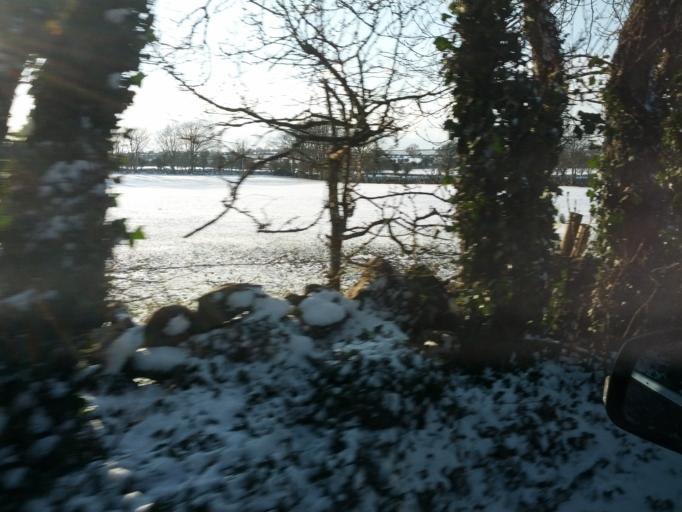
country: IE
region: Connaught
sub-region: County Galway
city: Athenry
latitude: 53.1960
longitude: -8.7358
